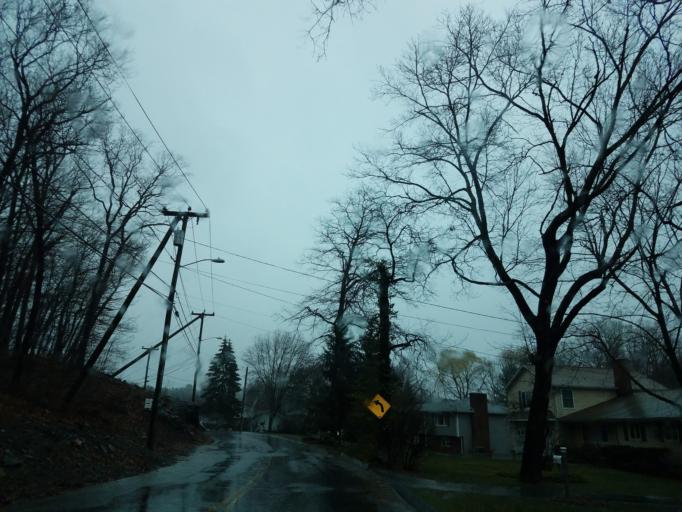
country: US
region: Connecticut
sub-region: New Haven County
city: Waterbury
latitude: 41.5373
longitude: -73.0784
